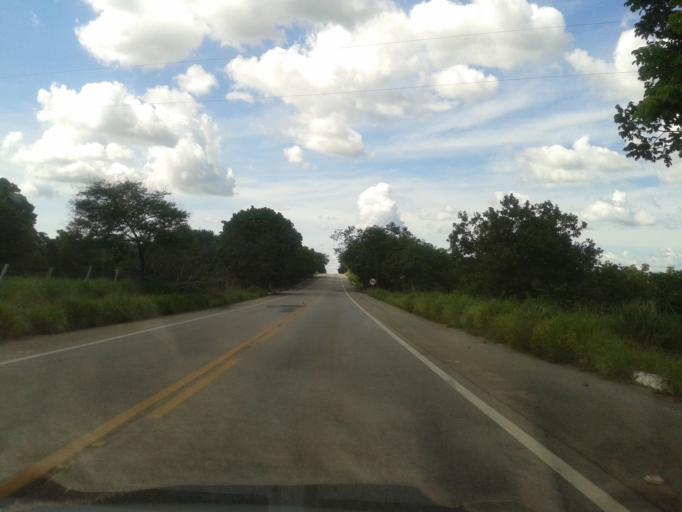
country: BR
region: Goias
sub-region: Itapuranga
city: Itapuranga
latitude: -15.5416
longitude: -50.2895
